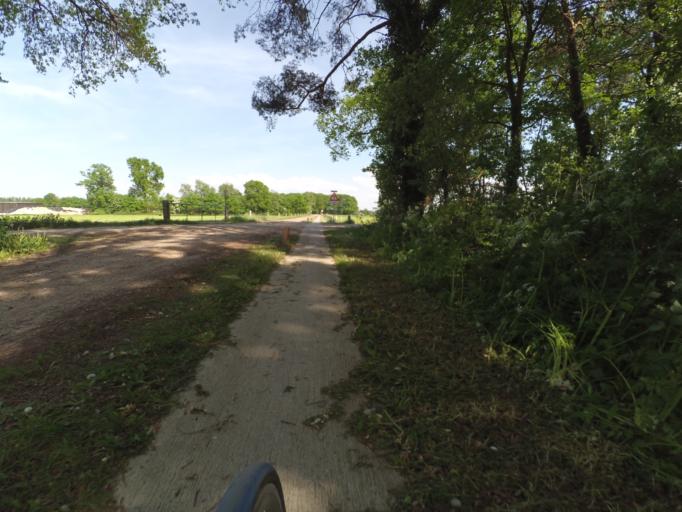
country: NL
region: Overijssel
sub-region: Gemeente Borne
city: Borne
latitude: 52.3464
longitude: 6.7584
